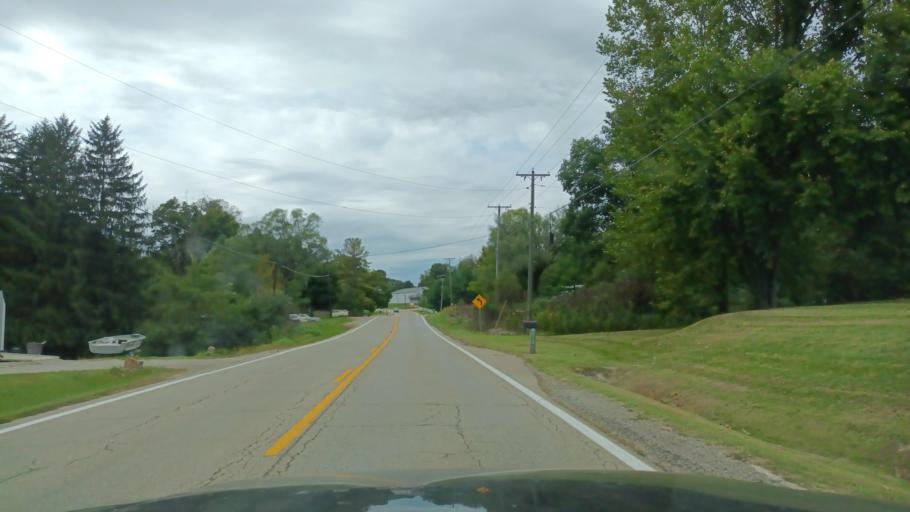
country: US
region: Ohio
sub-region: Vinton County
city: McArthur
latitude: 39.2611
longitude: -82.5057
